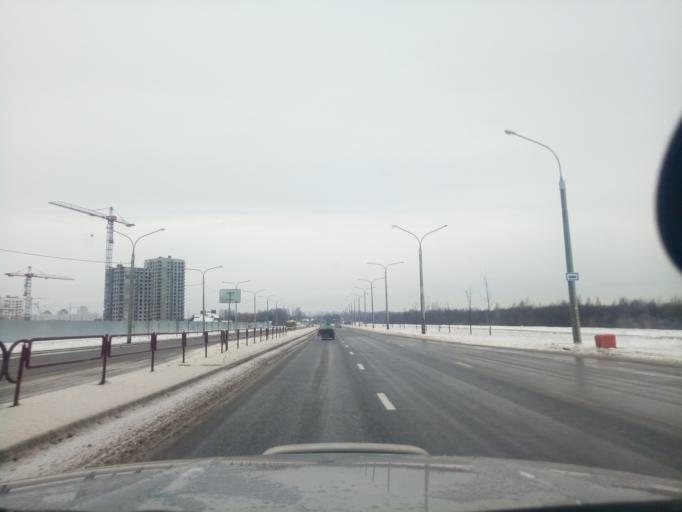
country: BY
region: Minsk
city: Machulishchy
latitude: 53.8374
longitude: 27.5981
